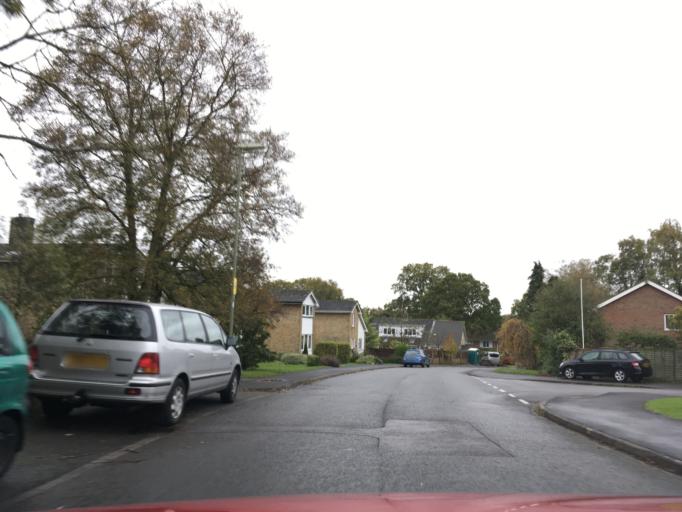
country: GB
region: England
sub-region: Hampshire
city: Colden Common
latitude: 50.9931
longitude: -1.3186
